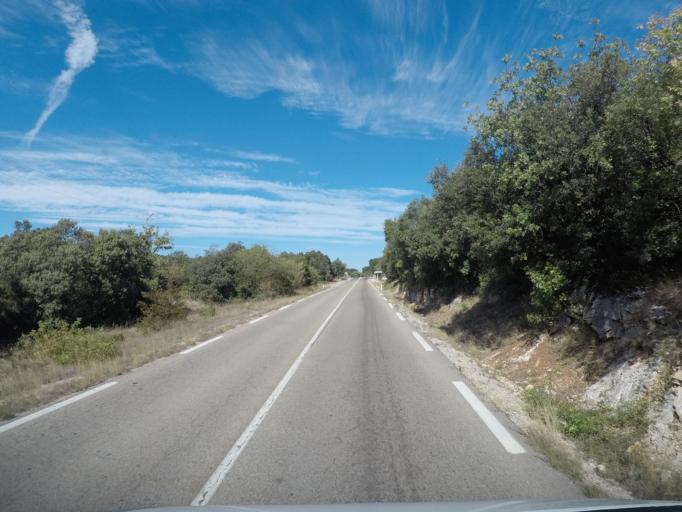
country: FR
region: Languedoc-Roussillon
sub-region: Departement de l'Herault
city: Saint-Martin-de-Londres
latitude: 43.7677
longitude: 3.7456
